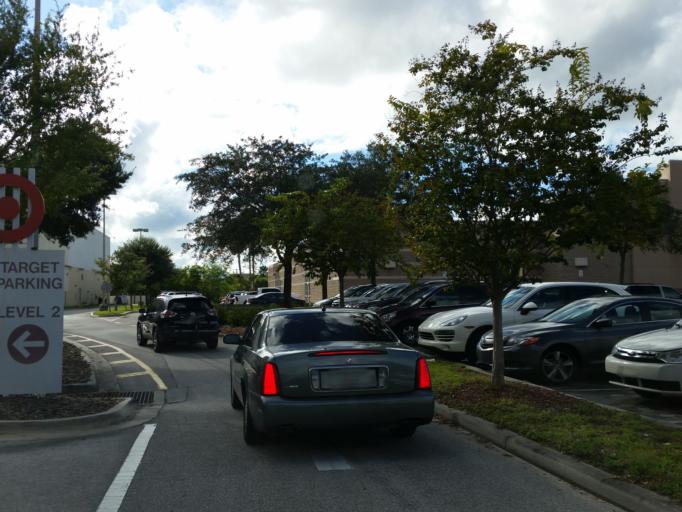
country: US
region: Florida
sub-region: Hillsborough County
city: Tampa
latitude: 27.9573
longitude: -82.5073
